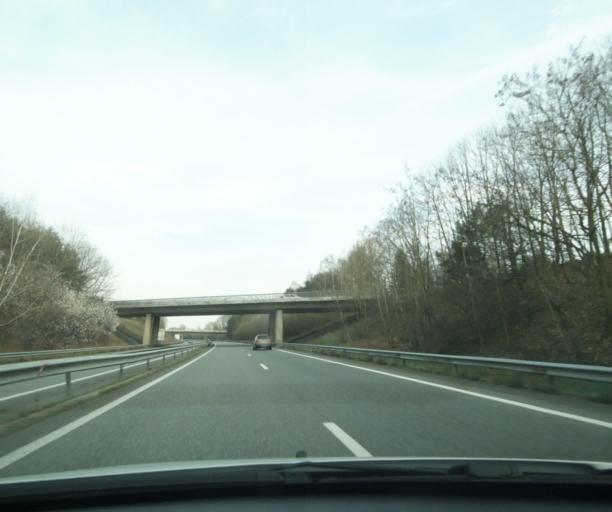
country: FR
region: Midi-Pyrenees
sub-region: Departement des Hautes-Pyrenees
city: Odos
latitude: 43.2090
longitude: 0.0446
